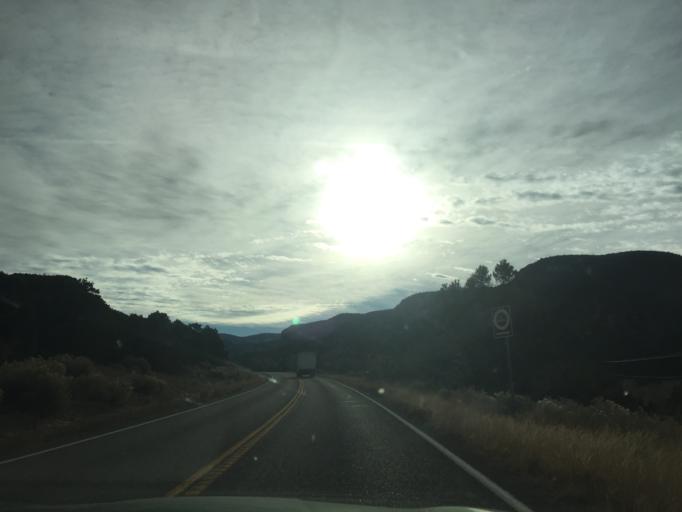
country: US
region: Utah
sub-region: Iron County
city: Cedar City
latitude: 37.6544
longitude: -112.9888
